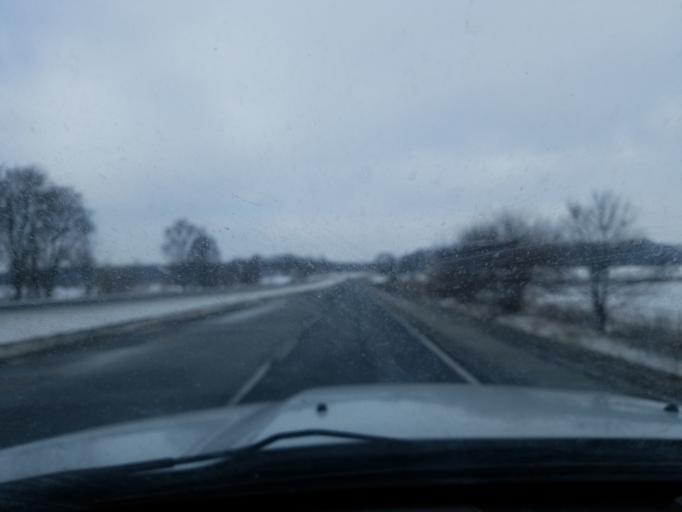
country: US
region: Indiana
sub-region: Marshall County
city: Plymouth
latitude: 41.2928
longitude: -86.2722
